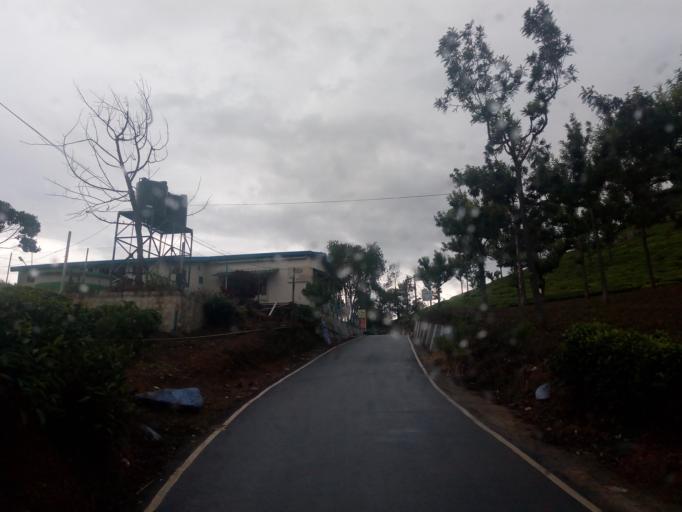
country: IN
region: Tamil Nadu
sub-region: Nilgiri
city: Kotagiri
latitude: 11.3661
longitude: 76.8546
